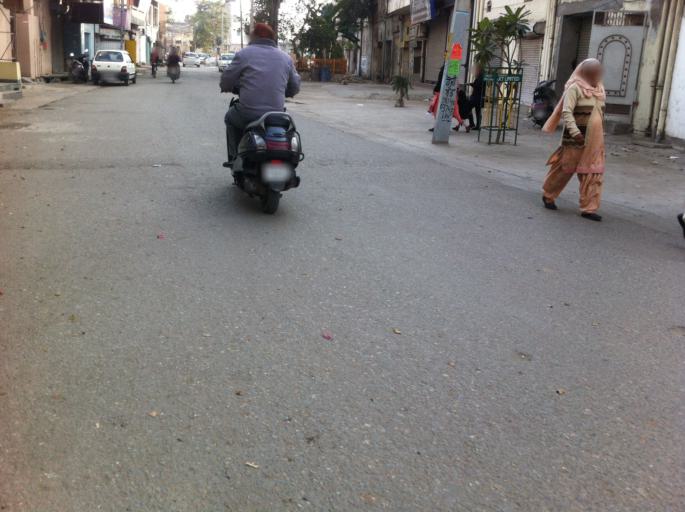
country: IN
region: Punjab
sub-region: Kapurthala
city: Phagwara
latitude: 31.2176
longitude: 75.7736
